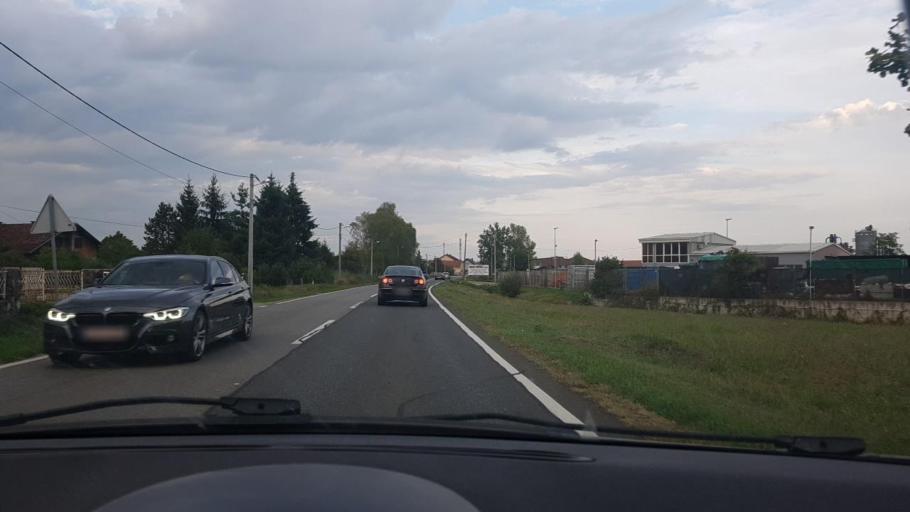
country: HR
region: Grad Zagreb
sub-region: Sesvete
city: Sesvete
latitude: 45.8792
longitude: 16.1691
